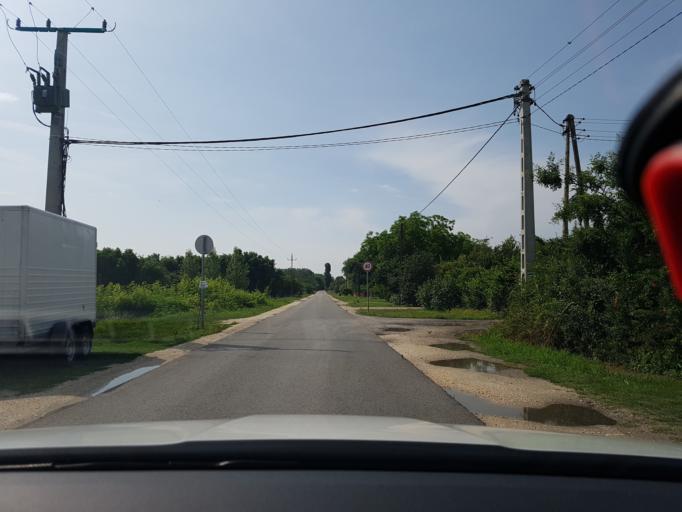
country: HU
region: Bacs-Kiskun
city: Kecskemet
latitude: 46.9245
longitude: 19.6452
